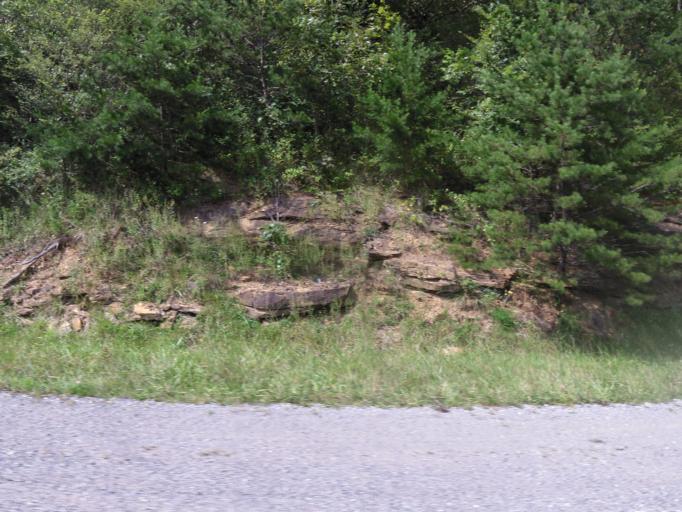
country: US
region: Kentucky
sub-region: Harlan County
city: Loyall
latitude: 36.8297
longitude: -83.4696
